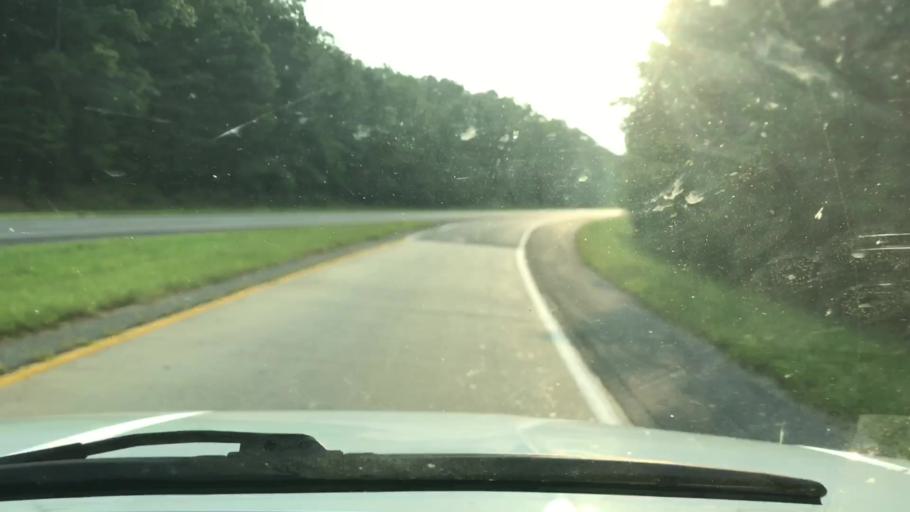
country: US
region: Virginia
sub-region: Chesterfield County
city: Chesterfield
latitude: 37.4100
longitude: -77.5699
